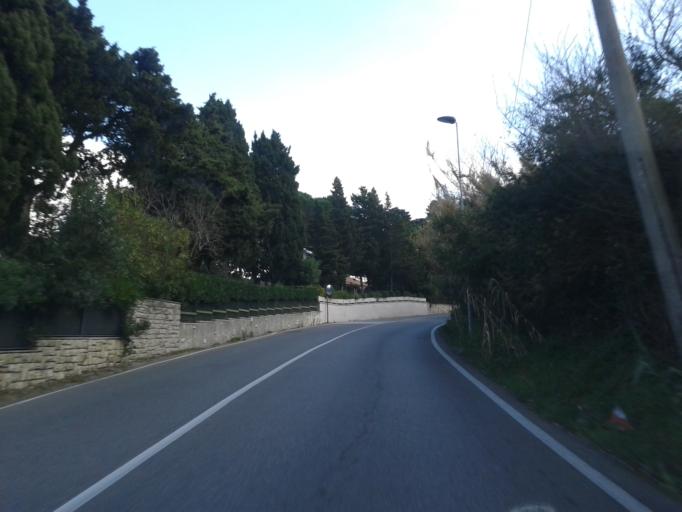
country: IT
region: Tuscany
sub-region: Provincia di Livorno
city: Livorno
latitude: 43.5058
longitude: 10.3371
